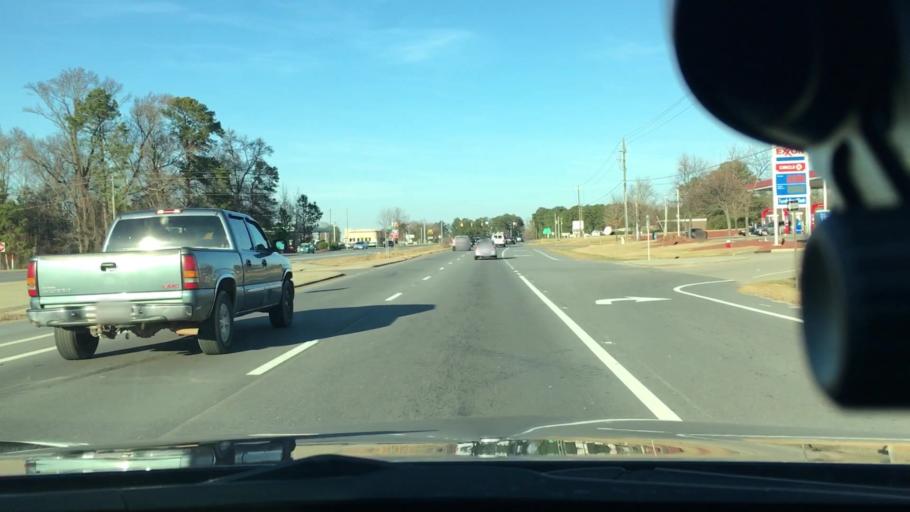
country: US
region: North Carolina
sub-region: Lee County
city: Sanford
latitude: 35.4384
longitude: -79.2168
